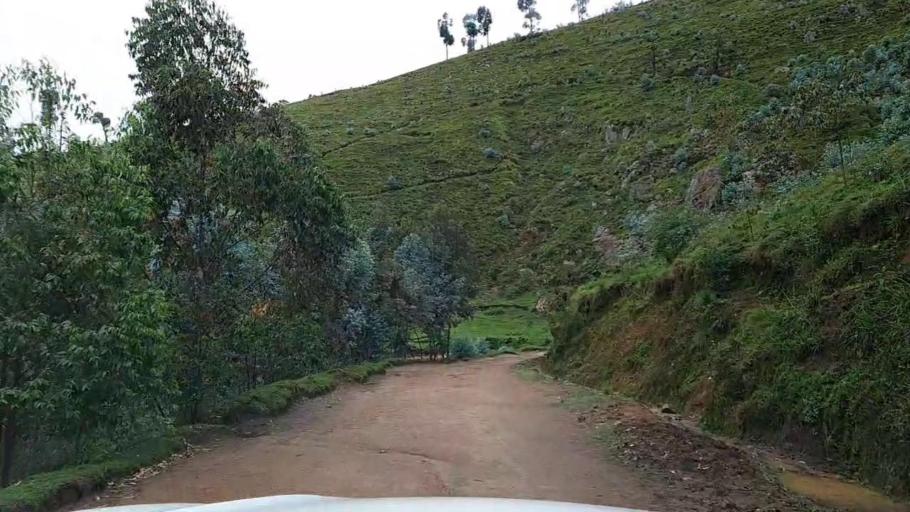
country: RW
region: Southern Province
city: Nzega
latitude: -2.3968
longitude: 29.5001
